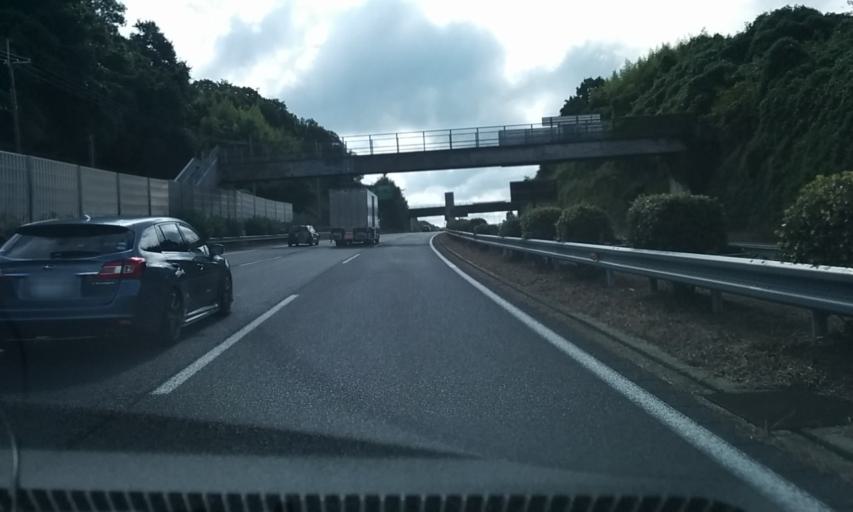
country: JP
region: Hyogo
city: Sandacho
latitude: 34.8903
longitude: 135.1595
